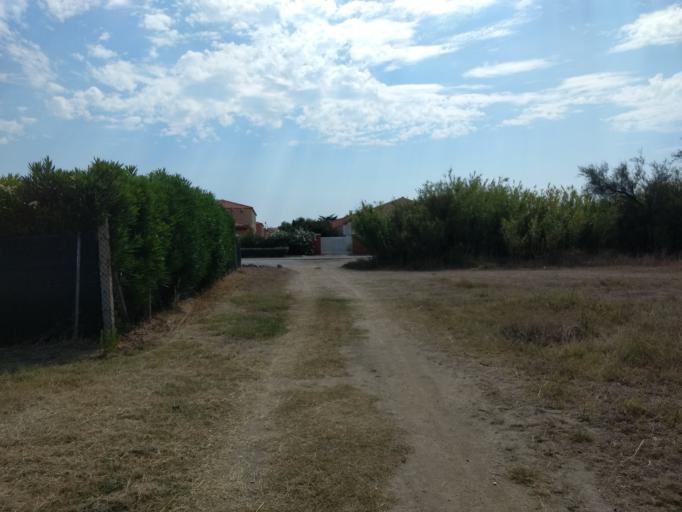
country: FR
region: Languedoc-Roussillon
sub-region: Departement des Pyrenees-Orientales
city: Le Barcares
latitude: 42.7909
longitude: 3.0299
